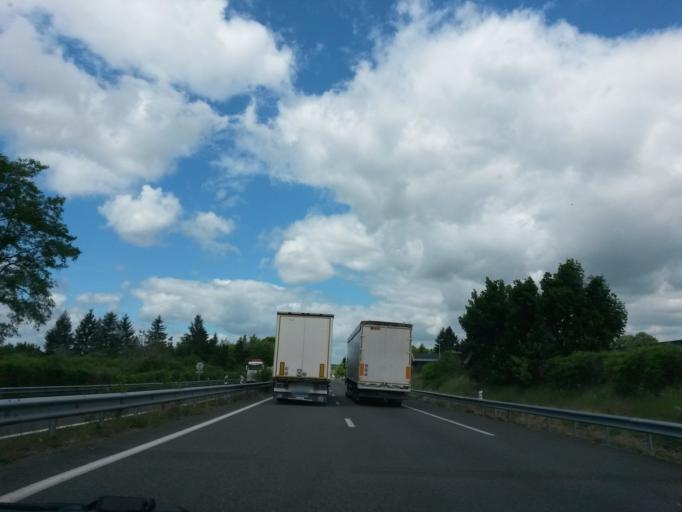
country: FR
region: Bourgogne
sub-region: Departement de la Nievre
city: Pouilly-sur-Loire
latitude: 47.2648
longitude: 2.9828
